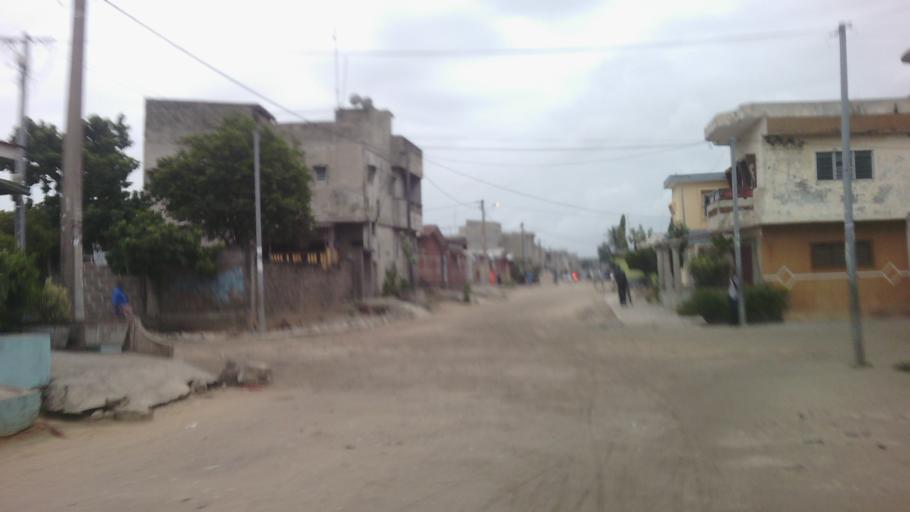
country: BJ
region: Atlantique
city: Abomey-Calavi
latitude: 6.3943
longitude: 2.3636
